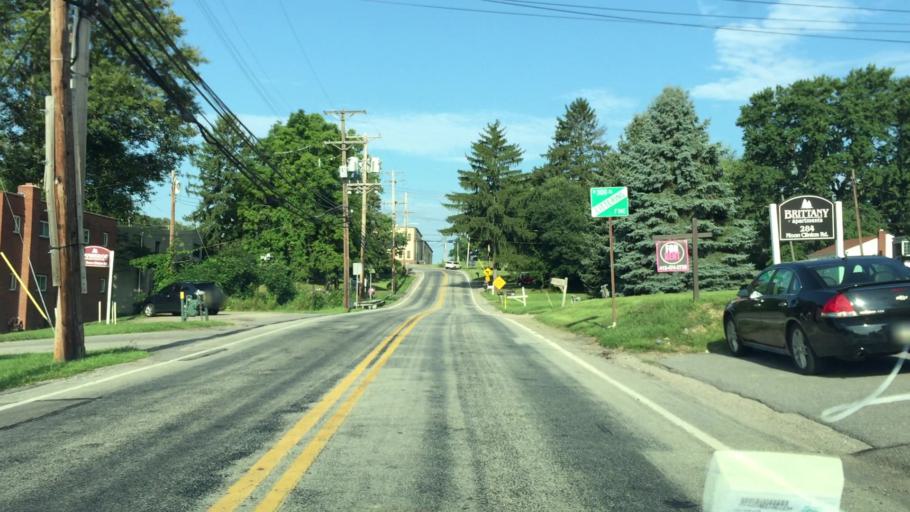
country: US
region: Pennsylvania
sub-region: Allegheny County
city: Carnot-Moon
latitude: 40.5130
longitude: -80.2310
